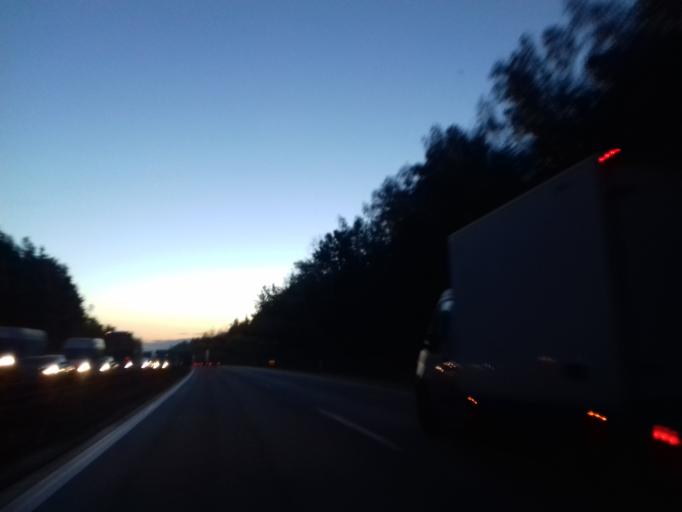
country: CZ
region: South Moravian
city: Zbraslav
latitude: 49.2579
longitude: 16.3199
